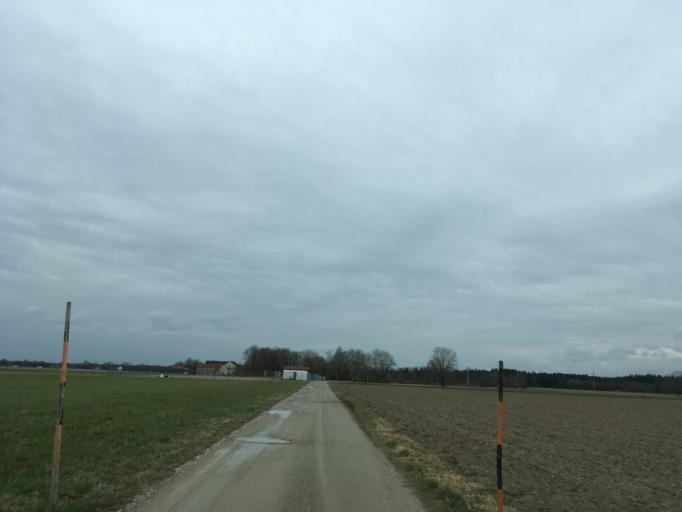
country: DE
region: Bavaria
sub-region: Upper Bavaria
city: Ampfing
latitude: 48.2387
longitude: 12.4057
